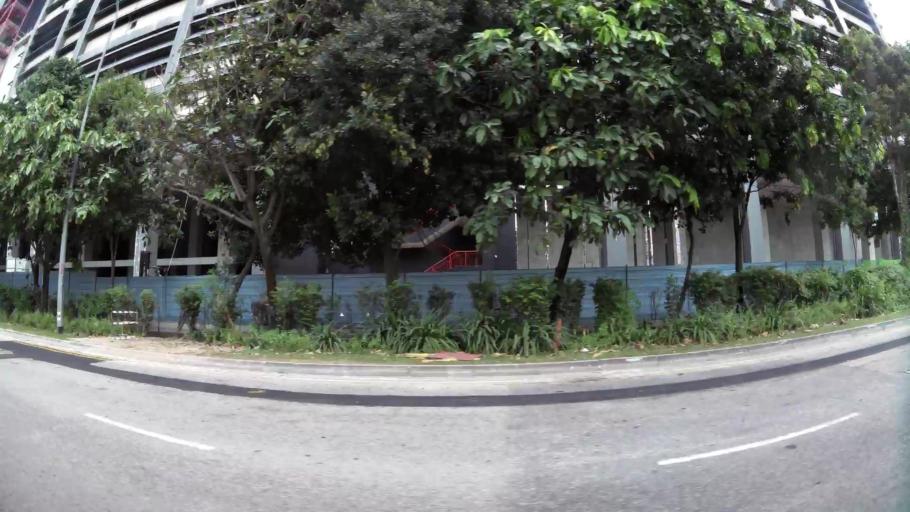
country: SG
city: Singapore
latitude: 1.3147
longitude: 103.7171
